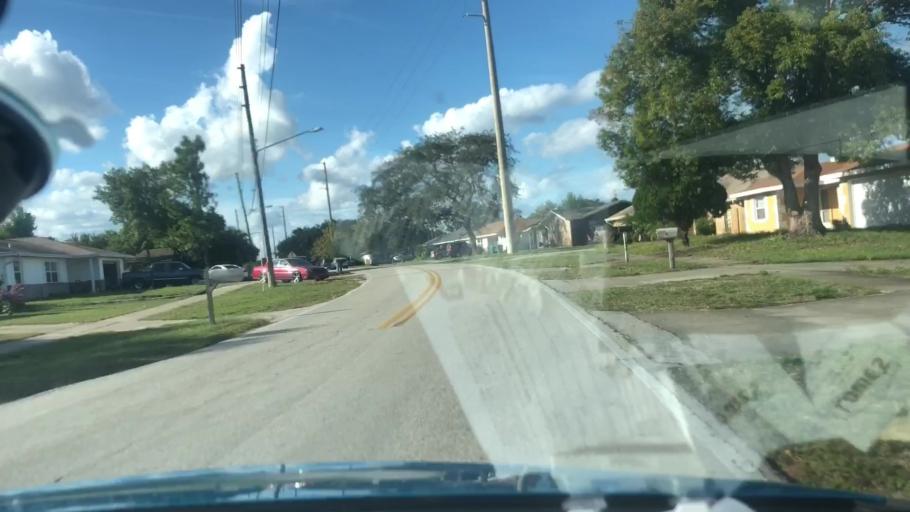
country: US
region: Florida
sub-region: Volusia County
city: Deltona
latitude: 28.8986
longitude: -81.2361
